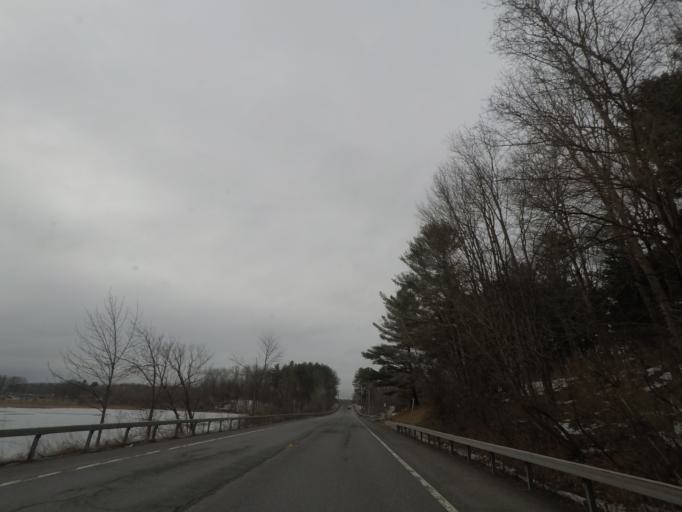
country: US
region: New York
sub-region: Schenectady County
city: Rotterdam
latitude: 42.7328
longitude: -73.9792
